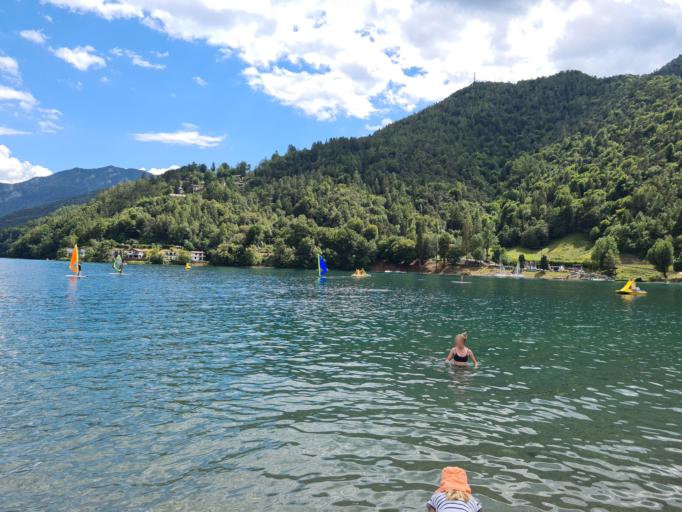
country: IT
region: Trentino-Alto Adige
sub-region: Provincia di Trento
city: Pieve di Ledro
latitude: 45.8850
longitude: 10.7345
